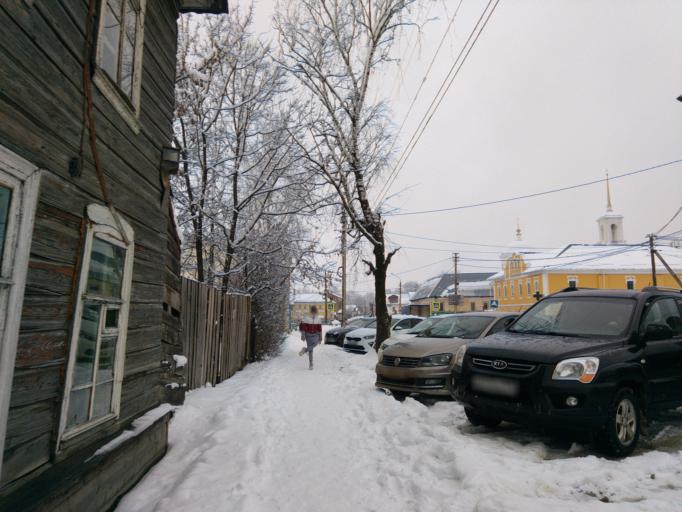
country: RU
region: Tverskaya
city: Torzhok
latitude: 57.0449
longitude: 34.9691
